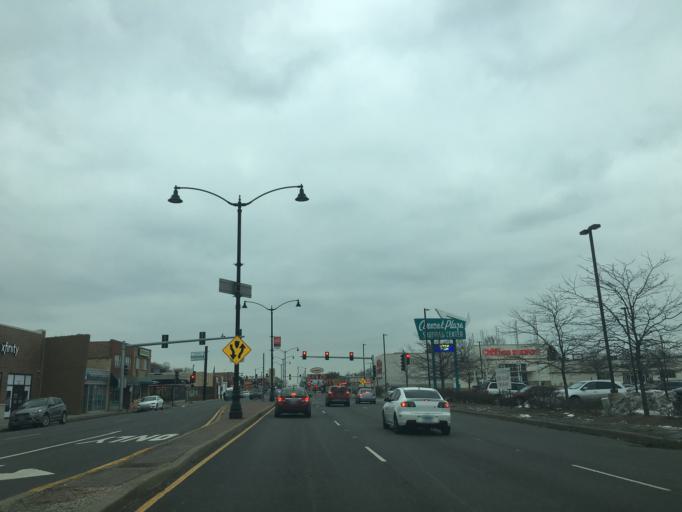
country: US
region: Illinois
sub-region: Cook County
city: Berwyn
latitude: 41.8504
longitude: -87.8011
